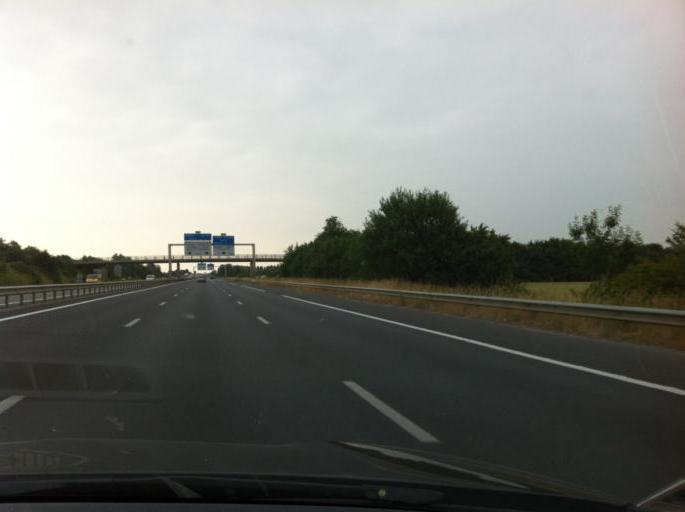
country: FR
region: Ile-de-France
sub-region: Departement de Seine-et-Marne
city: Vert-Saint-Denis
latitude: 48.5810
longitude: 2.6378
